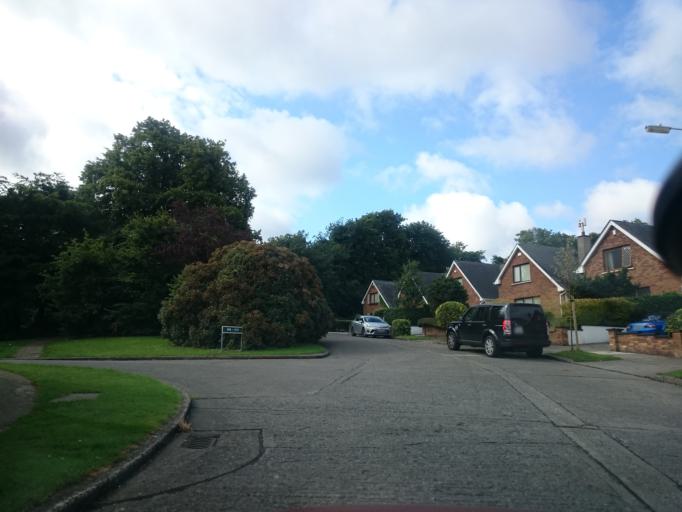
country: IE
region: Leinster
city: Mount Merrion
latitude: 53.2850
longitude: -6.2052
